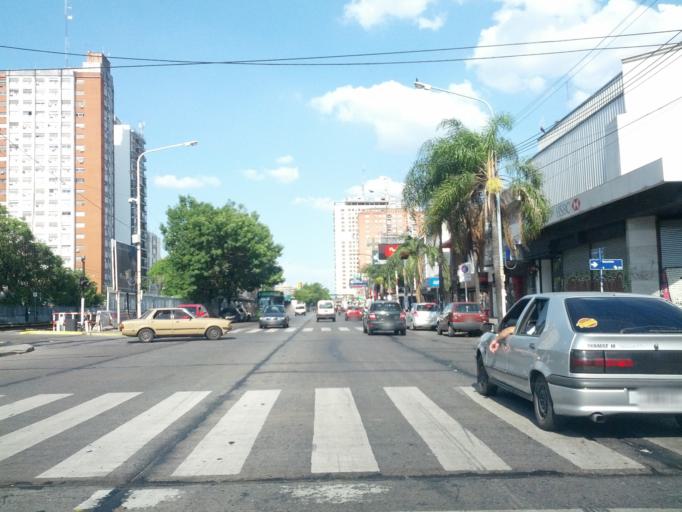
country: AR
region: Buenos Aires
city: San Justo
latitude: -34.6412
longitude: -58.5675
